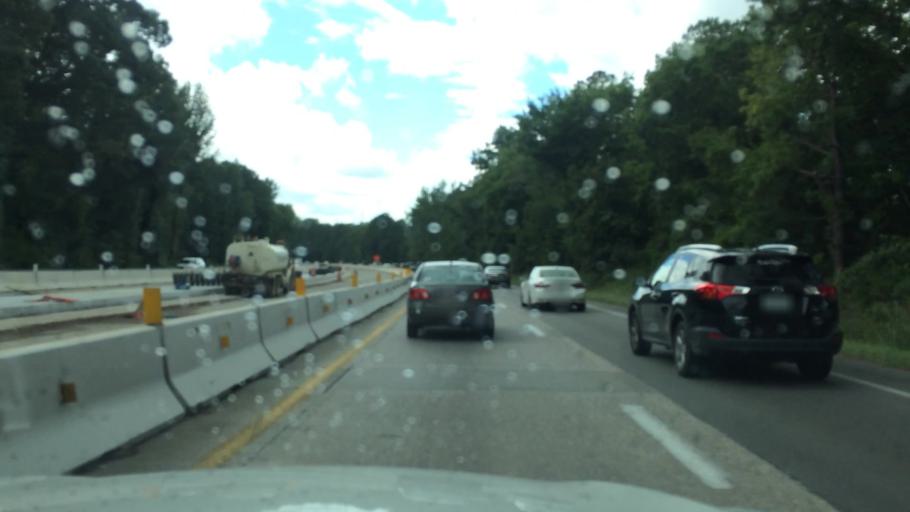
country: US
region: South Carolina
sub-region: Lexington County
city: Oak Grove
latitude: 34.0030
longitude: -81.1694
